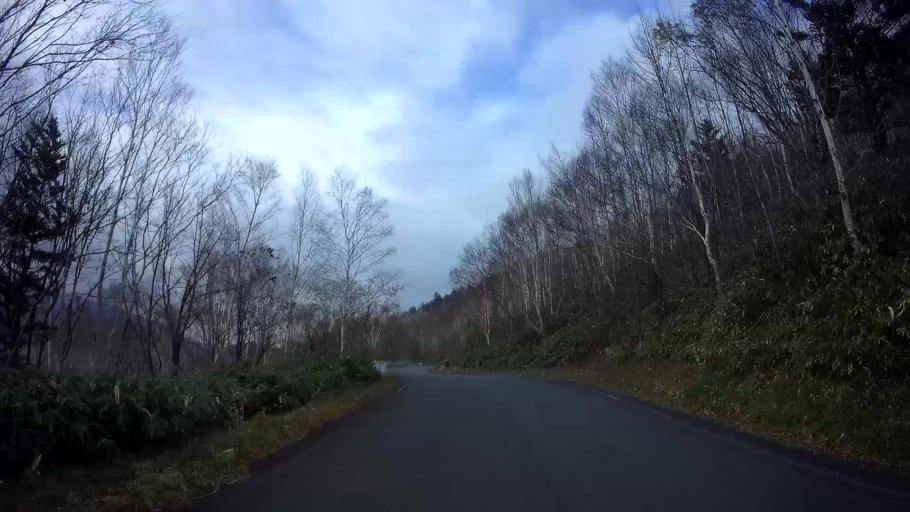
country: JP
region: Gunma
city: Nakanojomachi
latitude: 36.7020
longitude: 138.6541
